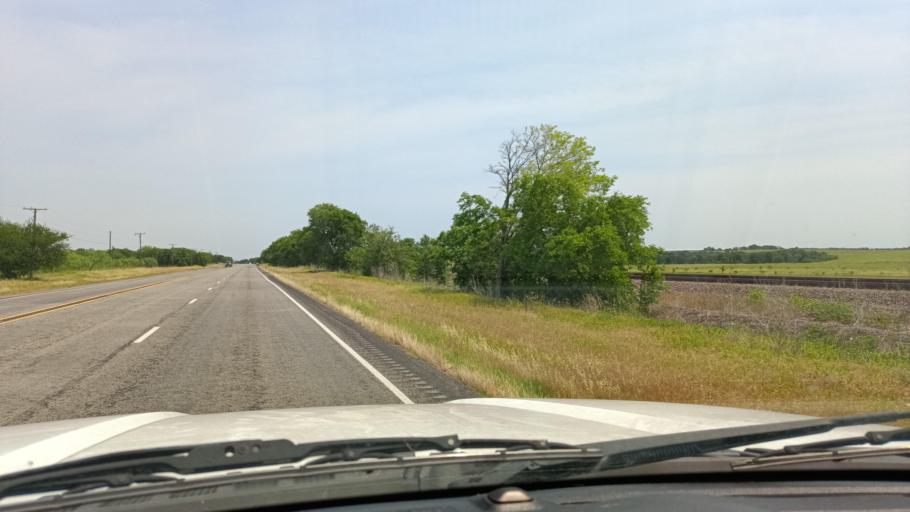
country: US
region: Texas
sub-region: Bell County
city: Rogers
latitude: 30.8667
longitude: -97.1170
